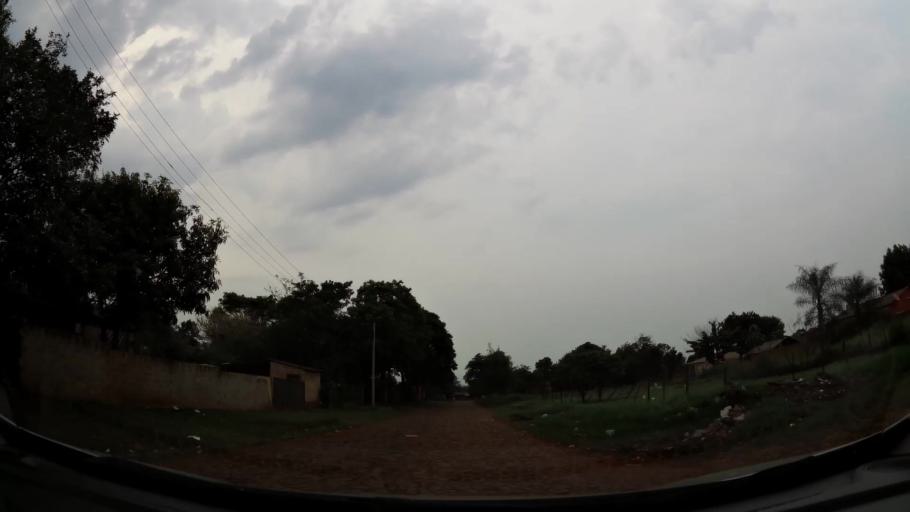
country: PY
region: Alto Parana
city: Presidente Franco
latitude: -25.5538
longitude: -54.6528
